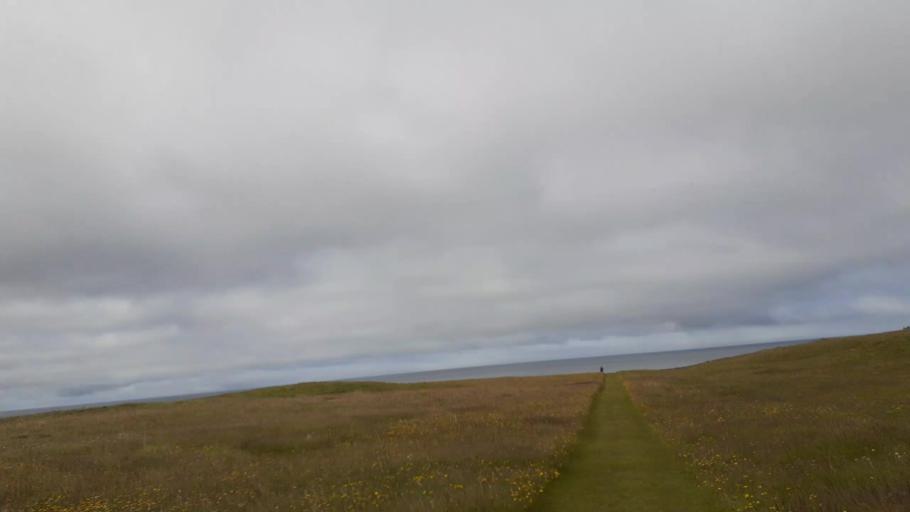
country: IS
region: Northeast
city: Dalvik
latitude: 66.5488
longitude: -18.0226
